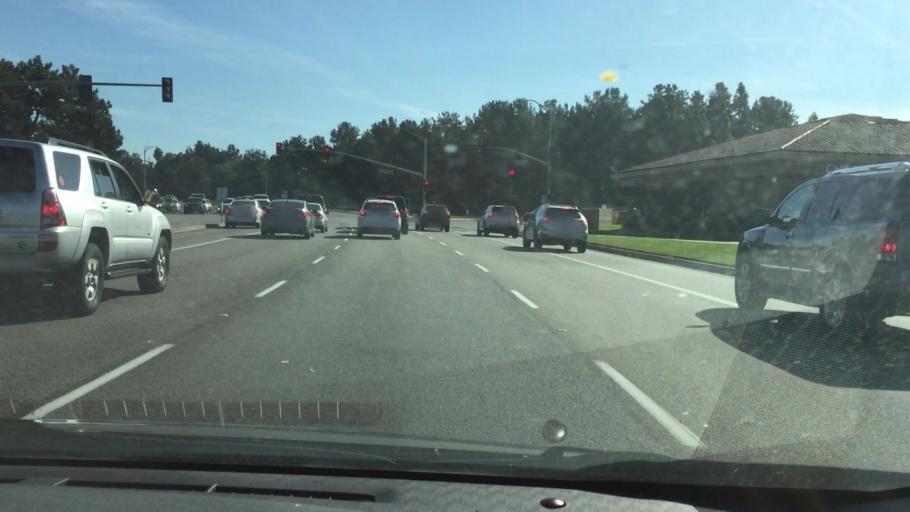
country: US
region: California
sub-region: Orange County
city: Portola Hills
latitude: 33.6519
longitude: -117.6452
